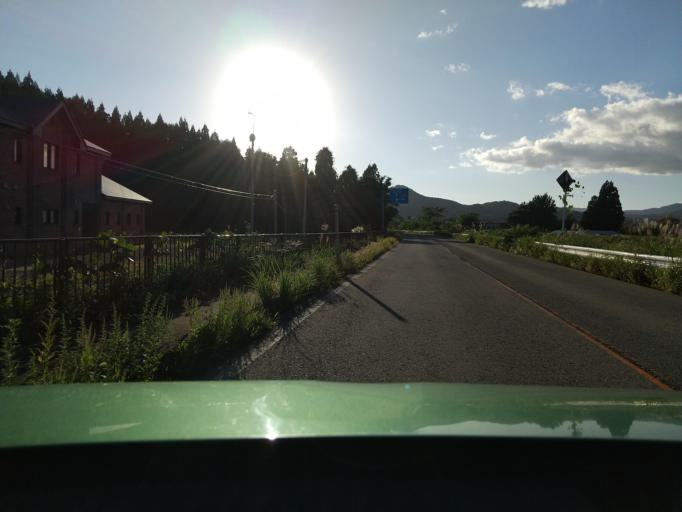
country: JP
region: Akita
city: Kakunodatemachi
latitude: 39.6098
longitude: 140.5739
